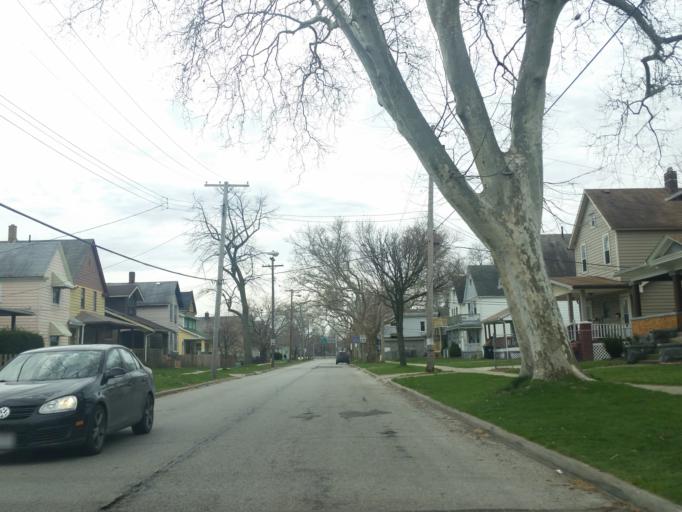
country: US
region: Ohio
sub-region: Cuyahoga County
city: Brooklyn
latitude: 41.4731
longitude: -81.7432
